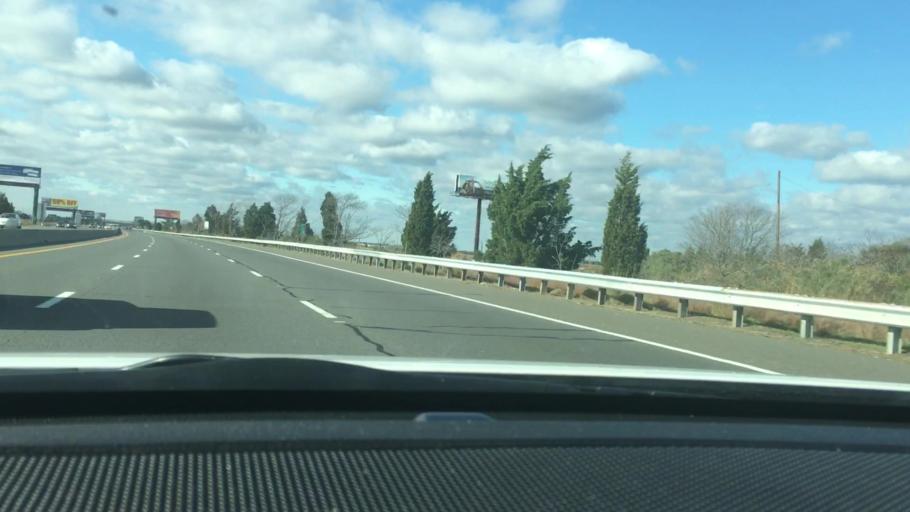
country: US
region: New Jersey
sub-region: Atlantic County
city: Ventnor City
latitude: 39.3699
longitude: -74.4647
